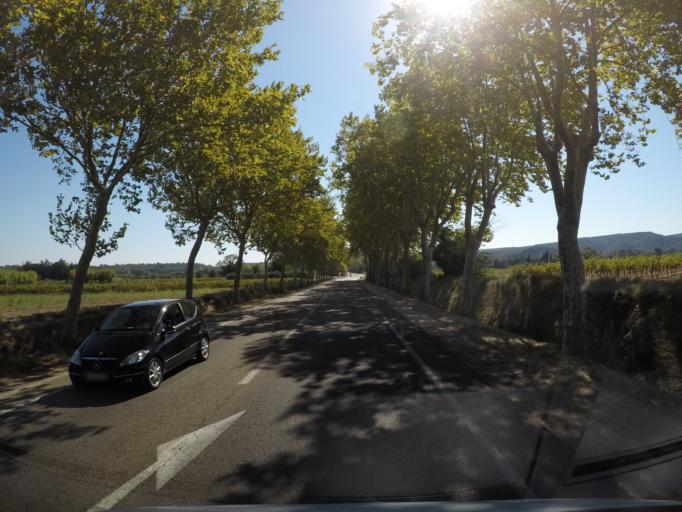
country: FR
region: Languedoc-Roussillon
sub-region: Departement du Gard
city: Castillon-du-Gard
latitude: 43.9618
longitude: 4.5160
